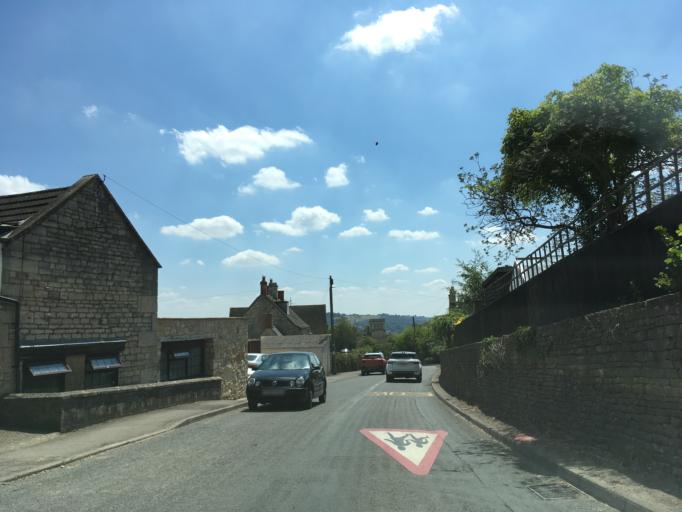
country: GB
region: England
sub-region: Gloucestershire
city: Stroud
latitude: 51.7622
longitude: -2.2332
